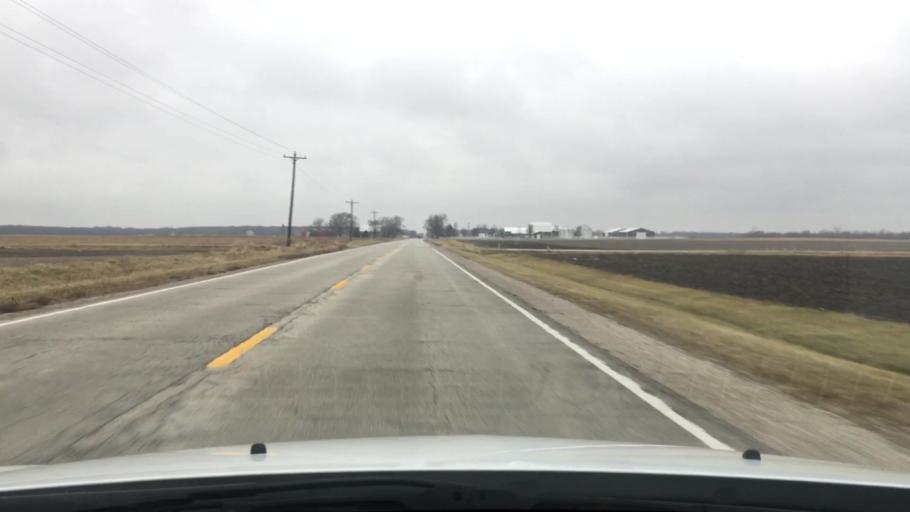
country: US
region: Illinois
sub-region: Iroquois County
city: Watseka
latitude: 40.8874
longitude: -87.8049
